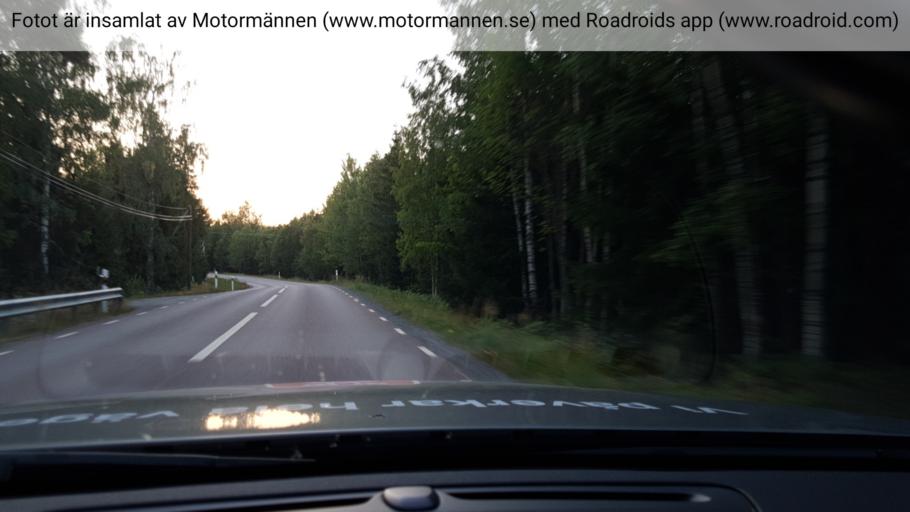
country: SE
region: Uppsala
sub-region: Heby Kommun
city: OEstervala
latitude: 60.0152
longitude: 17.2874
